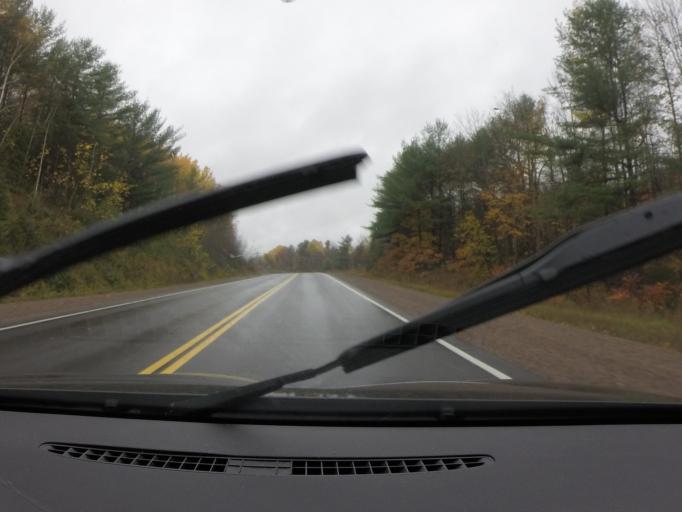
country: CA
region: Ontario
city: Skatepark
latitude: 44.7215
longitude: -76.9760
